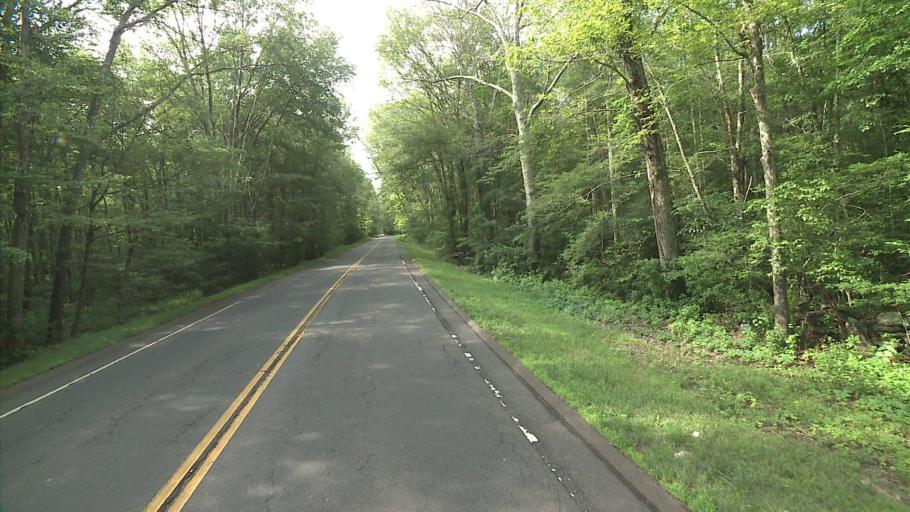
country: US
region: Connecticut
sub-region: Middlesex County
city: Clinton
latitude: 41.3385
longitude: -72.4934
